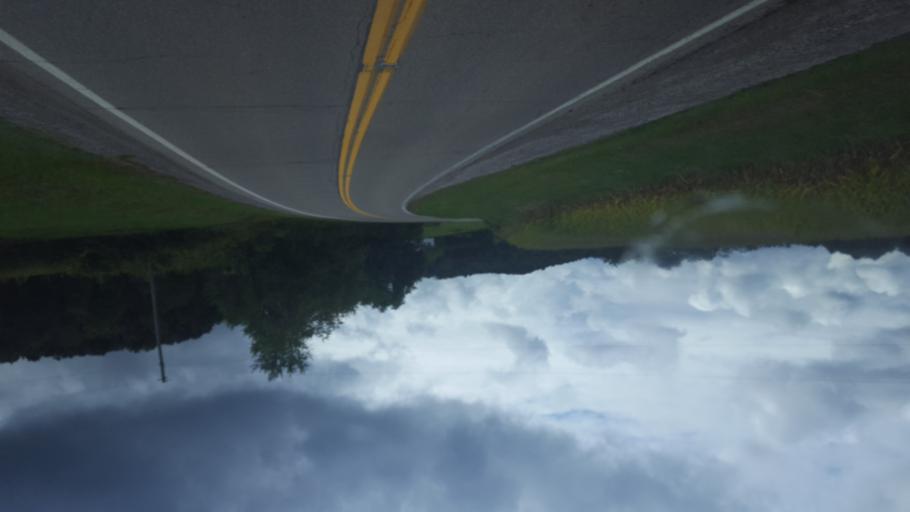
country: US
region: Ohio
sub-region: Jackson County
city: Oak Hill
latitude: 38.8835
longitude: -82.7443
